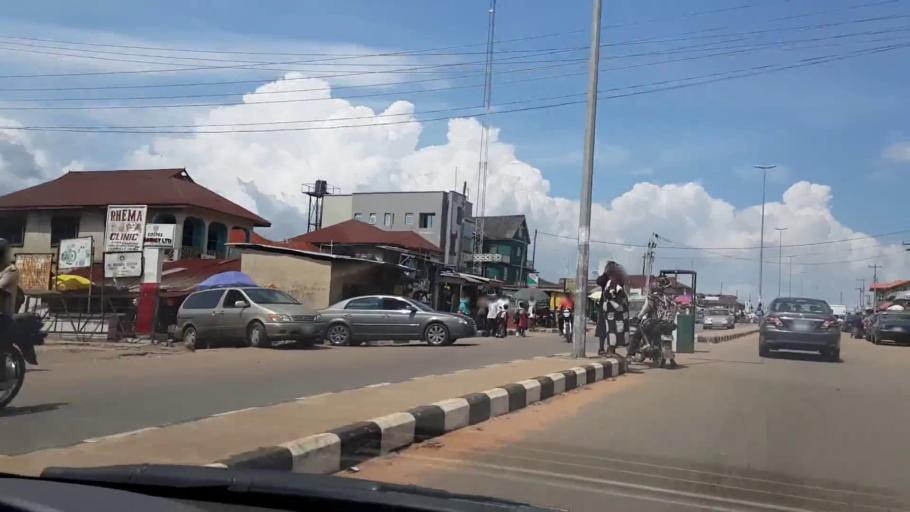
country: NG
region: Ondo
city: Ondo
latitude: 7.1003
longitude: 4.8433
